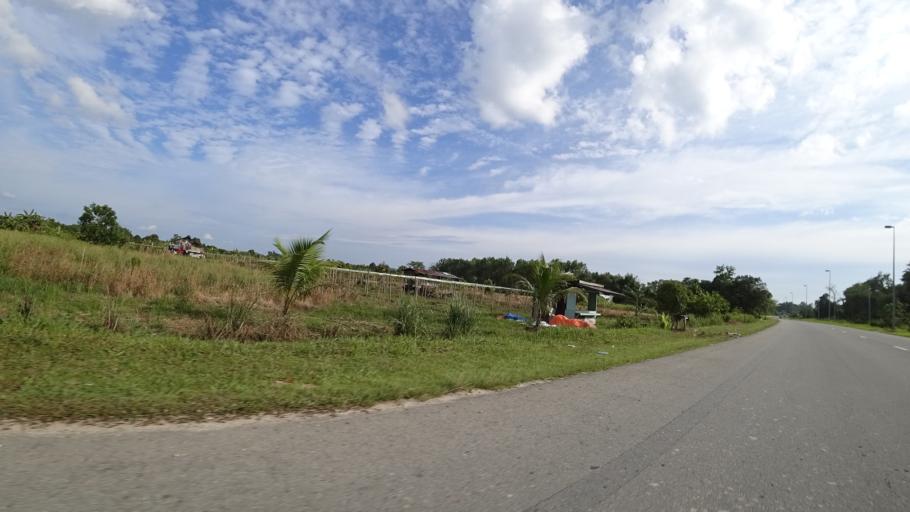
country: MY
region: Sarawak
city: Limbang
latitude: 4.7913
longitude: 114.8417
